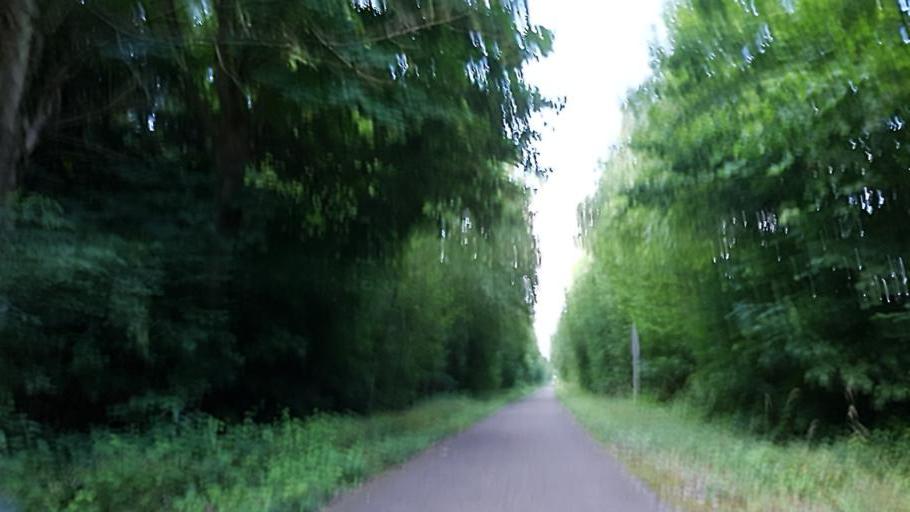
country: BE
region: Wallonia
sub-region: Province du Brabant Wallon
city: Court-Saint-Etienne
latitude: 50.6310
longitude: 4.5366
